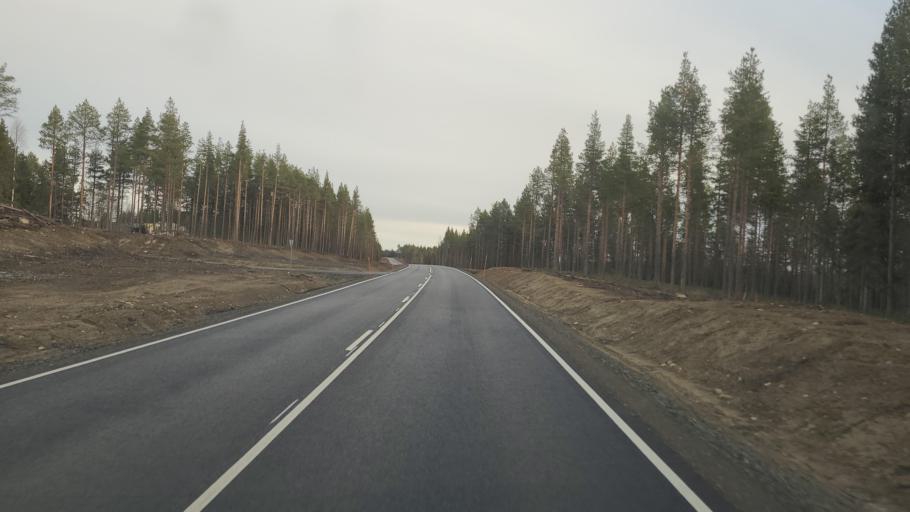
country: FI
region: Lapland
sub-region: Tunturi-Lappi
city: Kittilae
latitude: 67.8643
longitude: 24.9756
